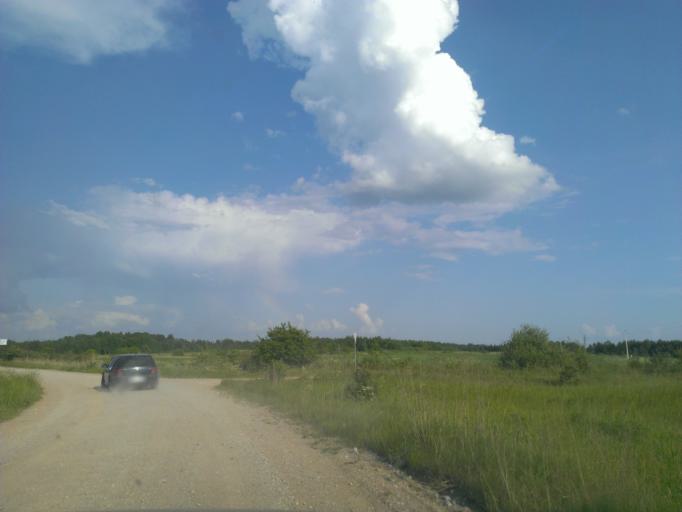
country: LT
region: Klaipedos apskritis
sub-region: Palanga
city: Sventoji
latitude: 56.0243
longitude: 21.2082
